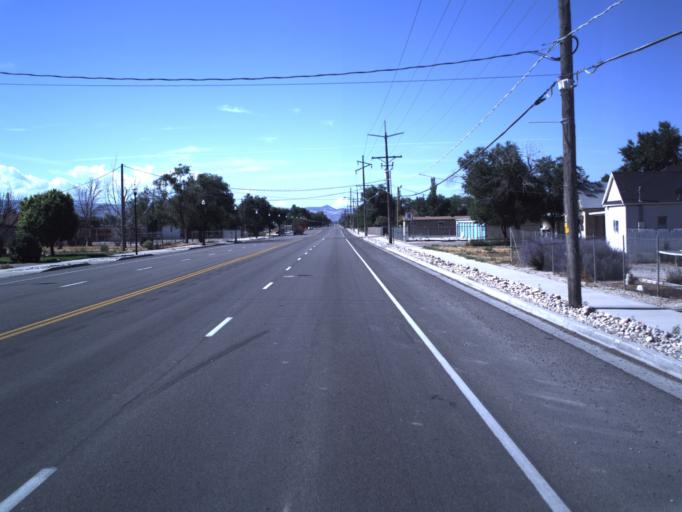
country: US
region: Utah
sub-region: Sanpete County
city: Centerfield
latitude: 39.1339
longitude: -111.8191
